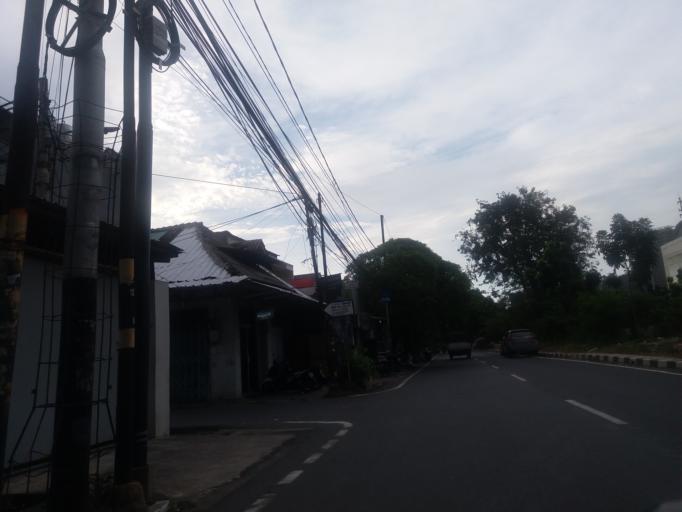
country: ID
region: Jakarta Raya
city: Jakarta
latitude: -6.1554
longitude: 106.8359
